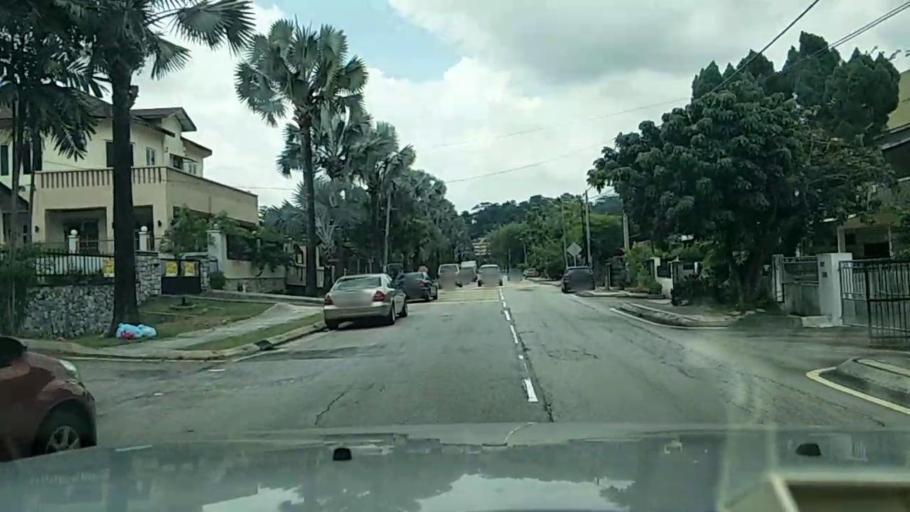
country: MY
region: Kuala Lumpur
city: Kuala Lumpur
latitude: 3.1340
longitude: 101.6734
